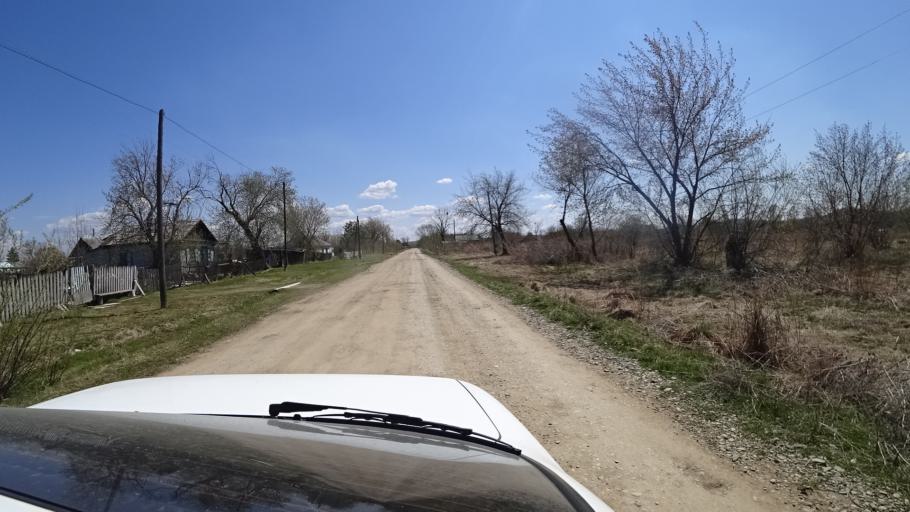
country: RU
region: Primorskiy
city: Dal'nerechensk
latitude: 45.8009
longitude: 133.7656
